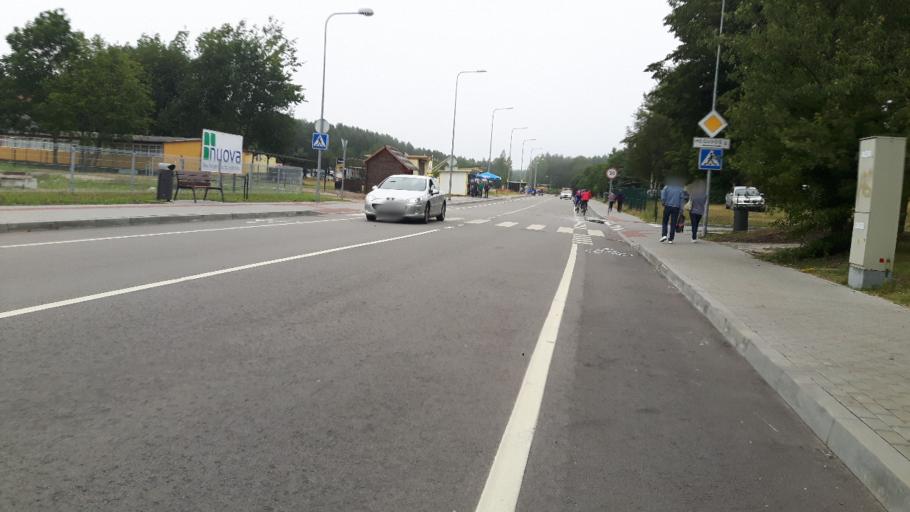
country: LT
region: Klaipedos apskritis
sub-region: Palanga
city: Sventoji
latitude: 56.0210
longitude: 21.0785
